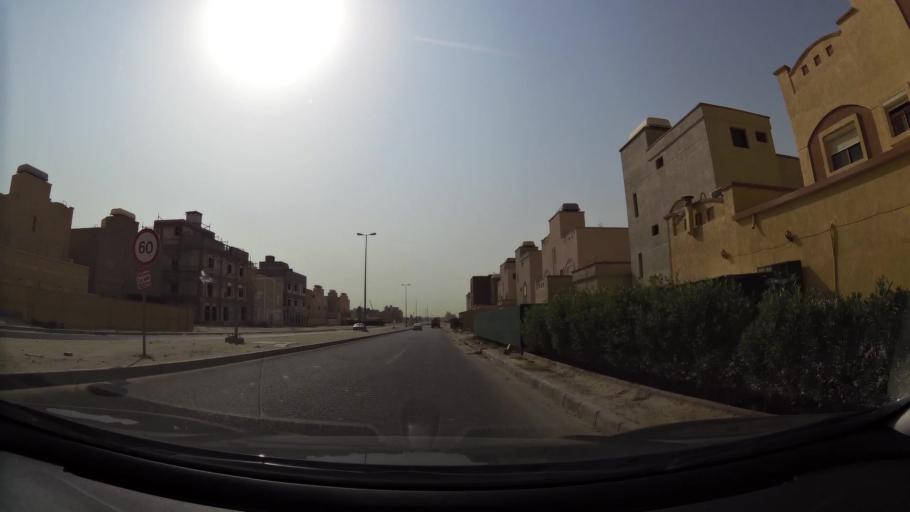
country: KW
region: Muhafazat al Jahra'
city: Al Jahra'
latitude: 29.3568
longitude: 47.7562
